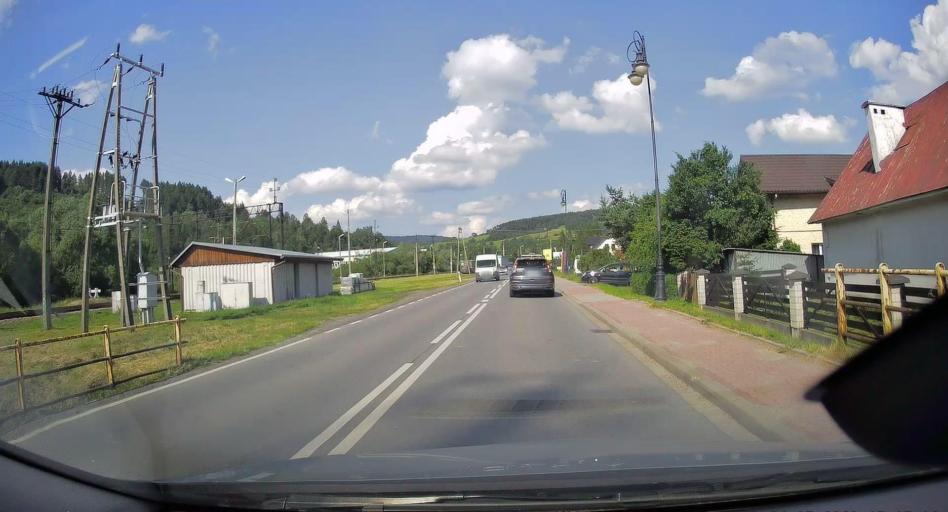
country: PL
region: Lesser Poland Voivodeship
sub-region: Powiat nowosadecki
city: Muszyna
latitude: 49.3693
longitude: 20.9428
